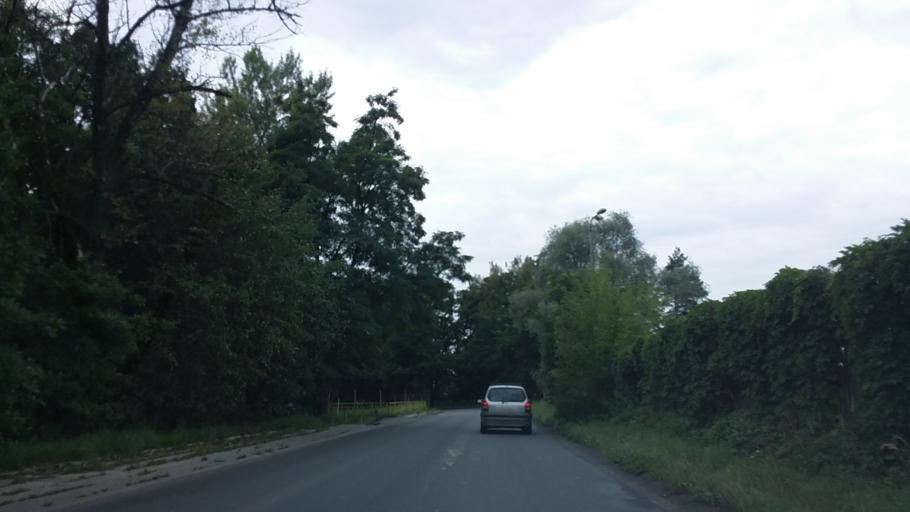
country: PL
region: Lesser Poland Voivodeship
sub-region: Powiat krakowski
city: Skawina
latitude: 49.9778
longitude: 19.8098
